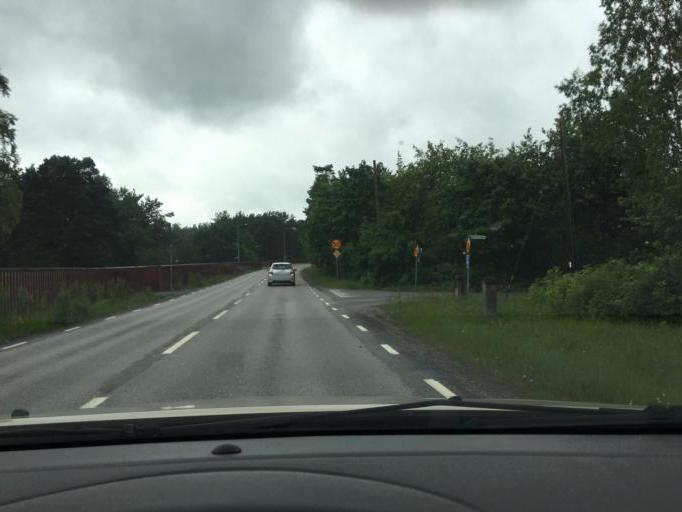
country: SE
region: Stockholm
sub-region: Varmdo Kommun
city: Hemmesta
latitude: 59.3246
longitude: 18.4952
